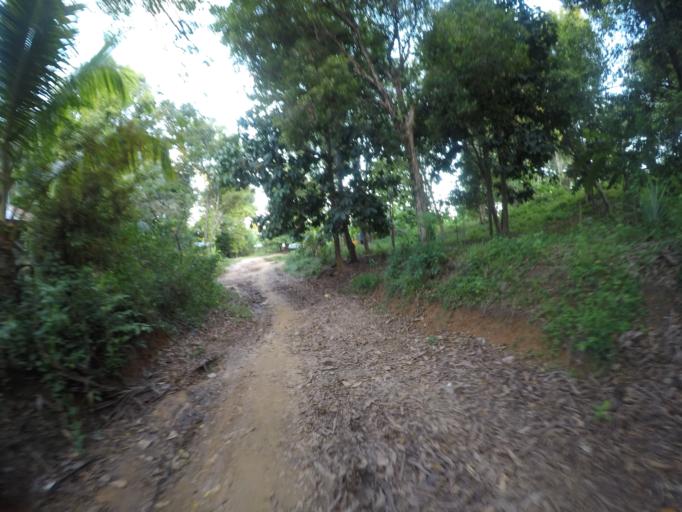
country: TZ
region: Pemba South
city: Mtambile
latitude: -5.3803
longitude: 39.7124
